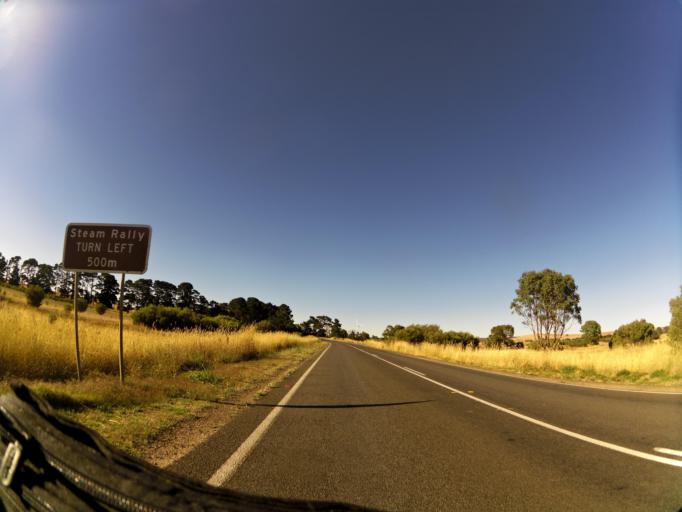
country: AU
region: Victoria
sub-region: Ballarat North
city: Delacombe
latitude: -37.5464
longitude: 143.3687
